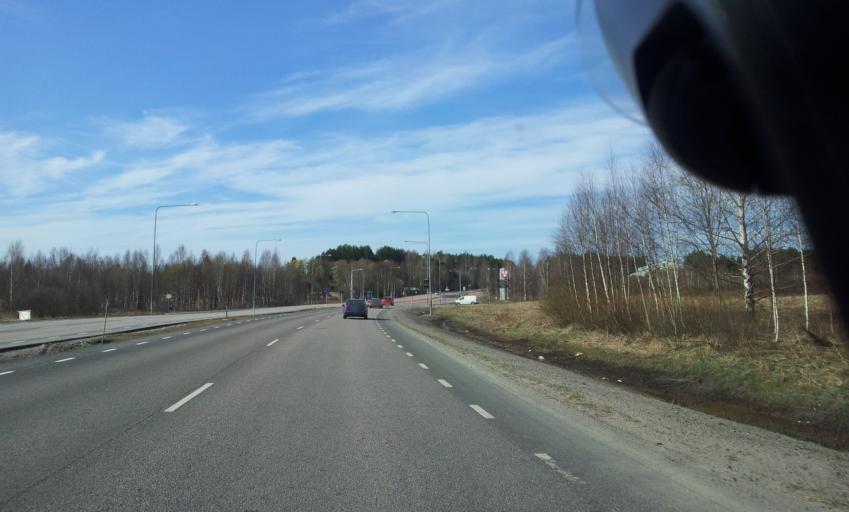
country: SE
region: Gaevleborg
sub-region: Hudiksvalls Kommun
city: Hudiksvall
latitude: 61.7150
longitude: 17.0890
